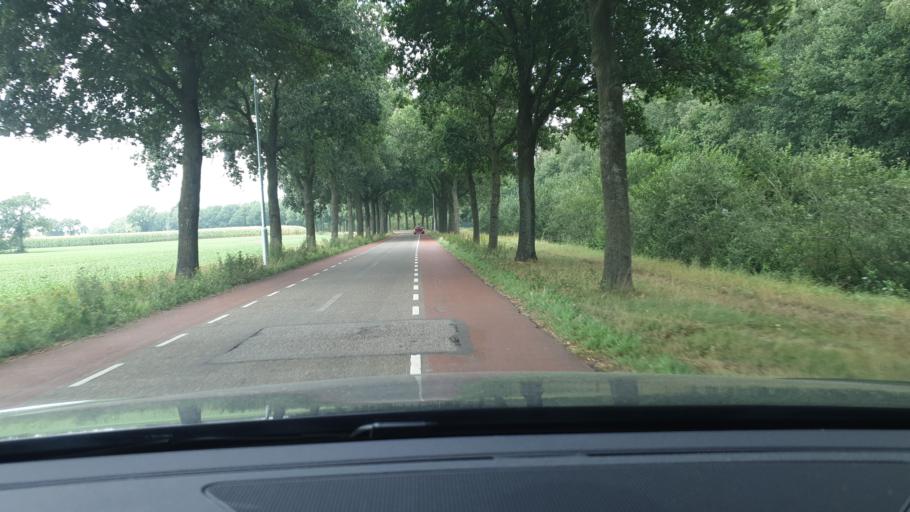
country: NL
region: North Brabant
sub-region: Gemeente Veldhoven
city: Oerle
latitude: 51.4473
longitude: 5.3614
